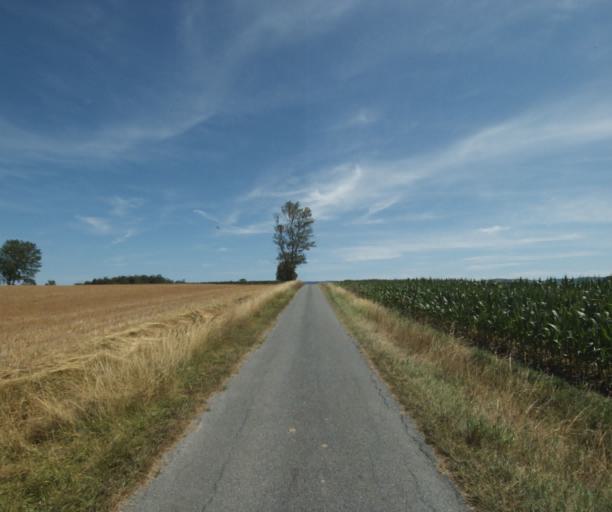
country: FR
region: Midi-Pyrenees
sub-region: Departement de la Haute-Garonne
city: Revel
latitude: 43.5102
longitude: 2.0144
